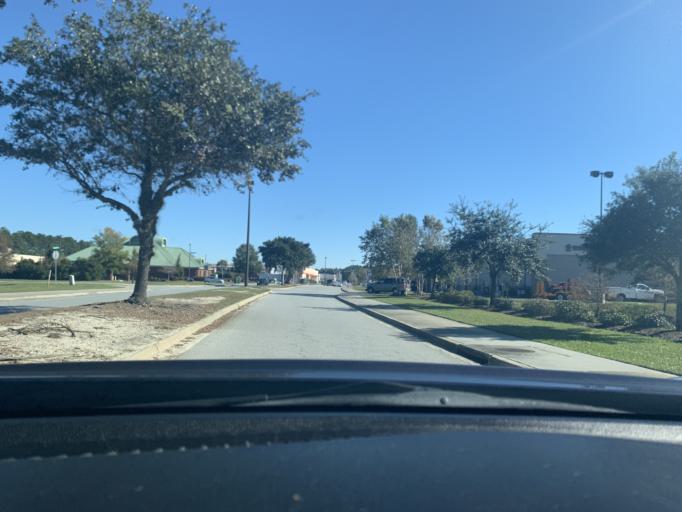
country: US
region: Georgia
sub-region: Chatham County
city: Pooler
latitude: 32.1429
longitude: -81.2495
